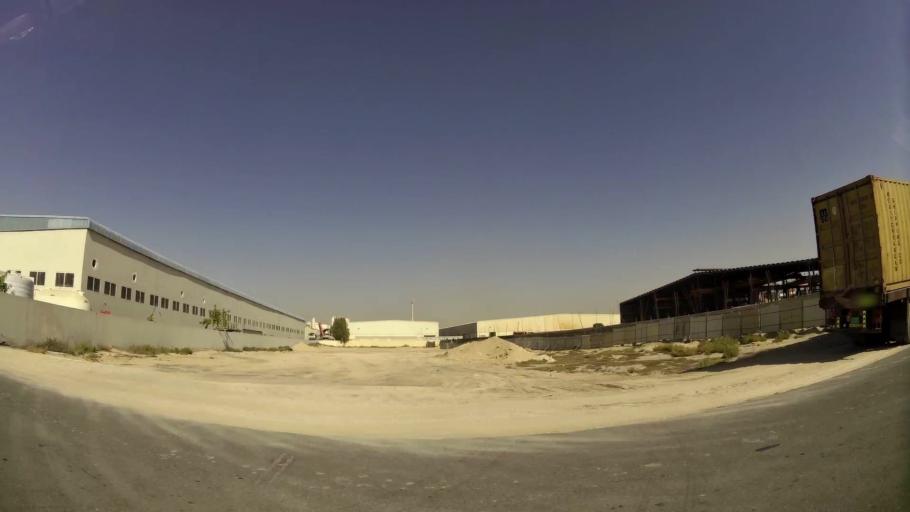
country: AE
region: Dubai
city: Dubai
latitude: 24.9898
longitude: 55.1067
